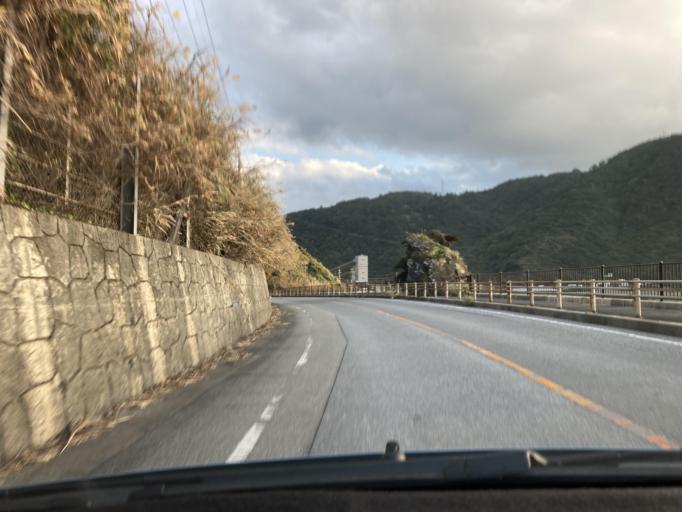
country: JP
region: Okinawa
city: Nago
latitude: 26.8013
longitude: 128.2314
